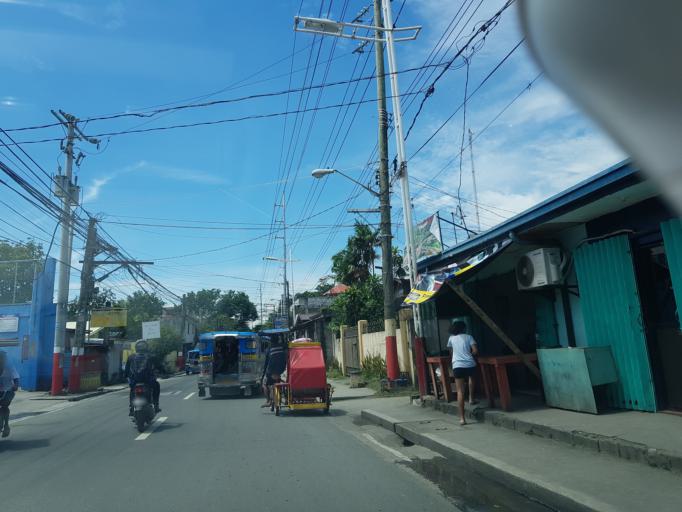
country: PH
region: Calabarzon
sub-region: Province of Rizal
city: Taguig
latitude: 14.5074
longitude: 121.0659
